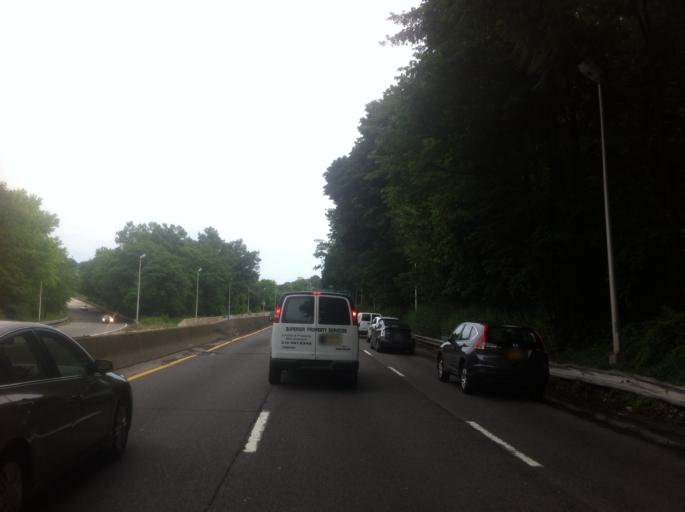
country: US
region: New York
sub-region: Nassau County
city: Great Neck Estates
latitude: 40.7589
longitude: -73.7497
